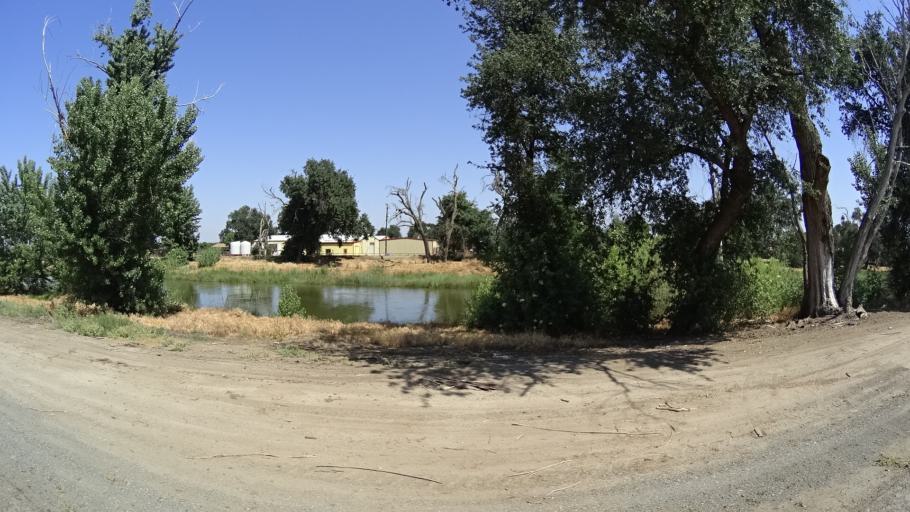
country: US
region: California
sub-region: Kings County
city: Lemoore
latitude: 36.3714
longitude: -119.7913
